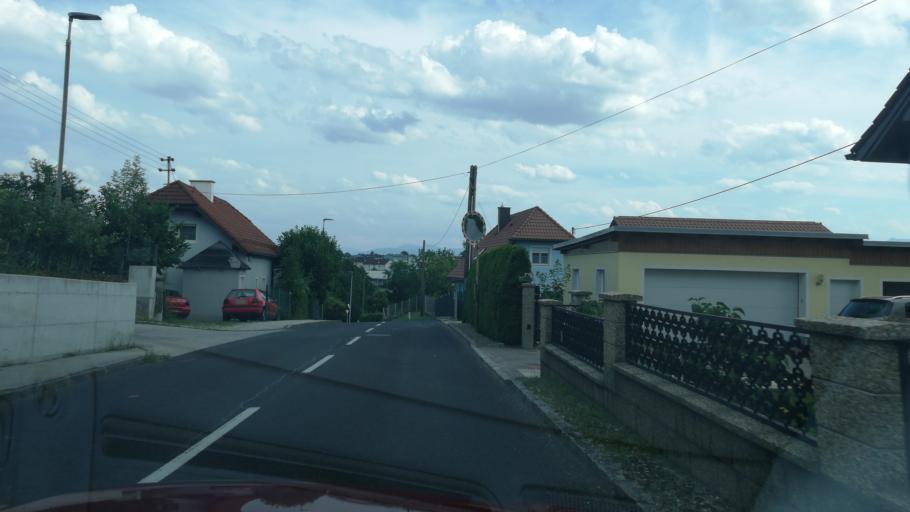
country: AT
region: Upper Austria
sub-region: Wels-Land
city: Lambach
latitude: 48.0975
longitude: 13.8634
